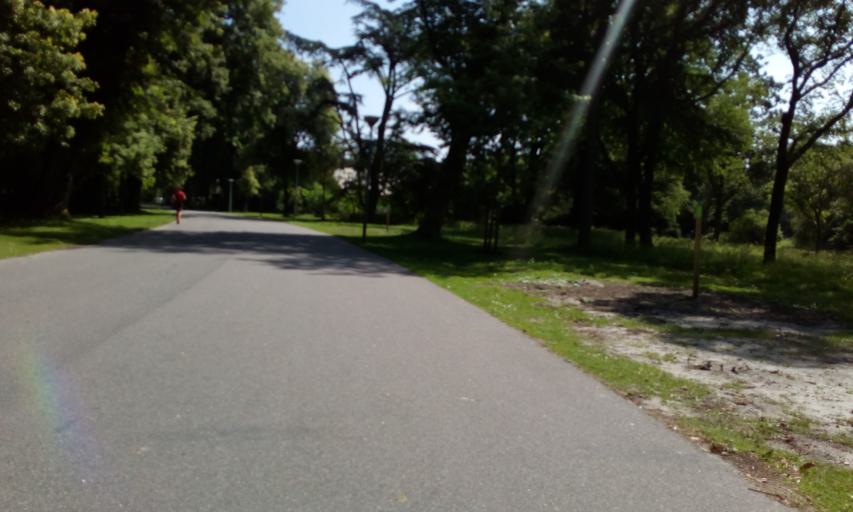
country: NL
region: South Holland
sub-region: Gemeente Den Haag
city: The Hague
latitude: 52.0527
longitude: 4.2849
